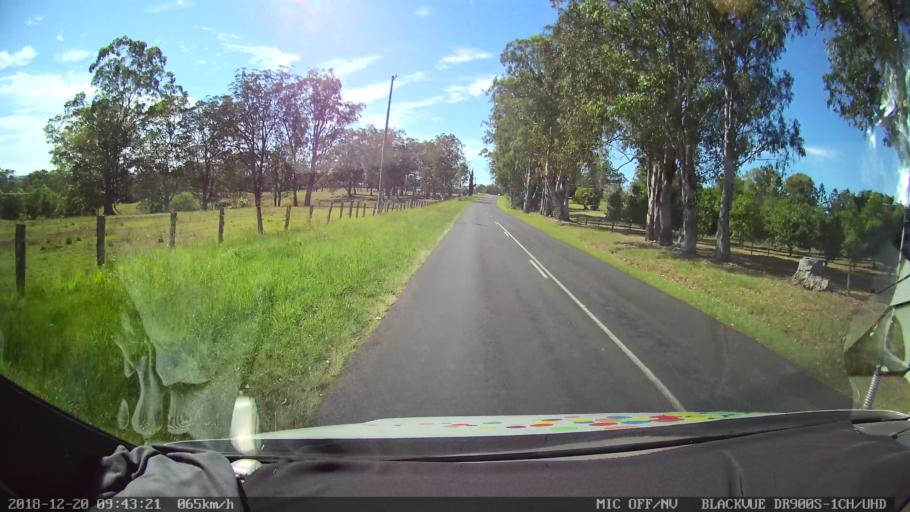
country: AU
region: New South Wales
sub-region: Lismore Municipality
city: Lismore
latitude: -28.7249
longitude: 153.2956
